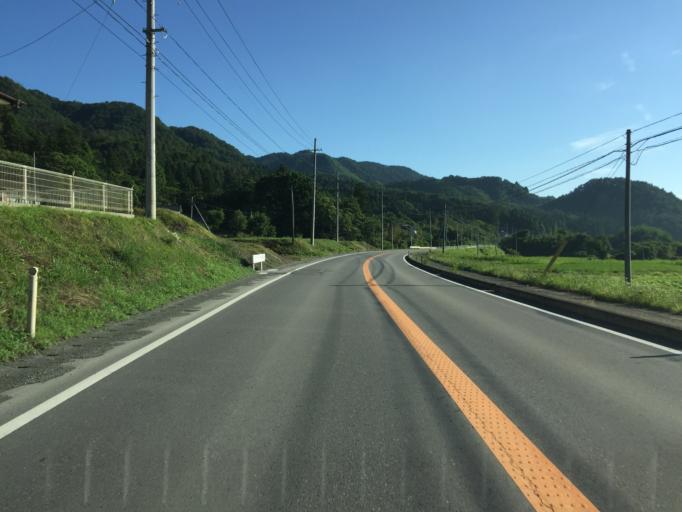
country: JP
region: Miyagi
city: Marumori
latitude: 37.7686
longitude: 140.8602
